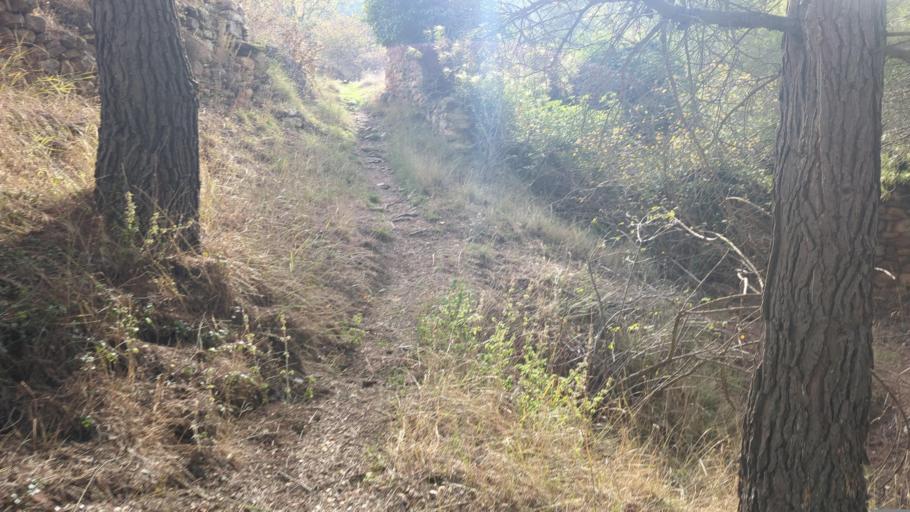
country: ES
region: La Rioja
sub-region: Provincia de La Rioja
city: Muro de Aguas
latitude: 42.1555
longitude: -2.1105
